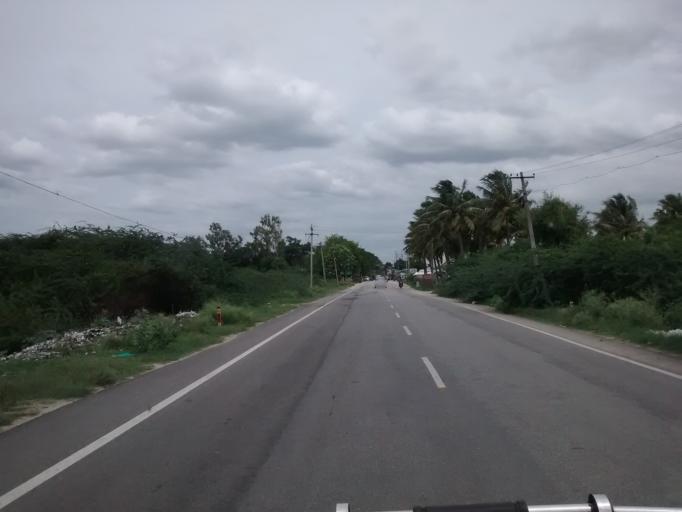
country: IN
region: Andhra Pradesh
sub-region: Chittoor
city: Chittoor
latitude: 13.2800
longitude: 79.0414
